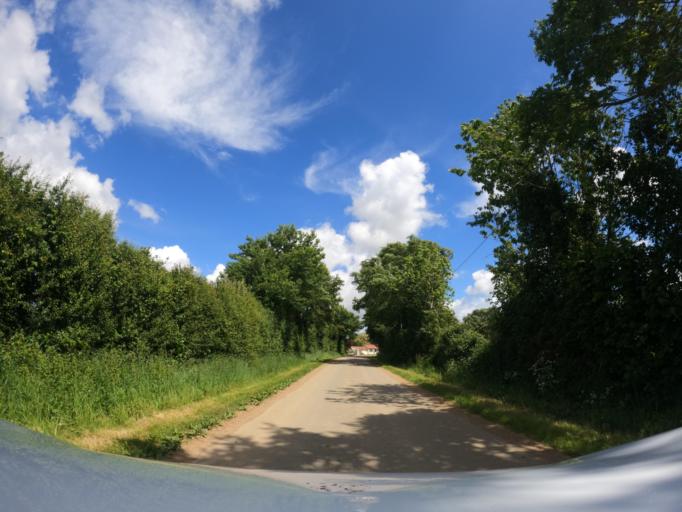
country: FR
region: Pays de la Loire
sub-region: Departement de la Vendee
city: Le Champ-Saint-Pere
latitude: 46.4760
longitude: -1.3097
